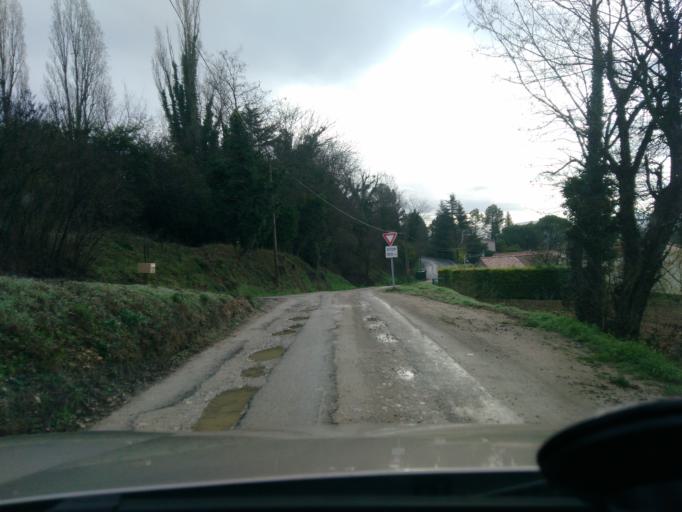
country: FR
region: Rhone-Alpes
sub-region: Departement de la Drome
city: Montboucher-sur-Jabron
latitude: 44.5501
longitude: 4.7989
